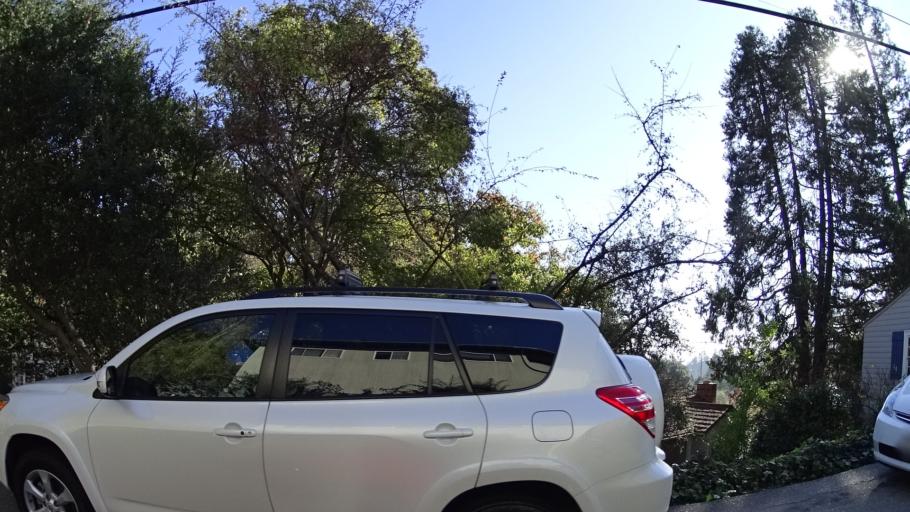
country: US
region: California
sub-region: Alameda County
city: Piedmont
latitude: 37.8291
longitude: -122.2078
